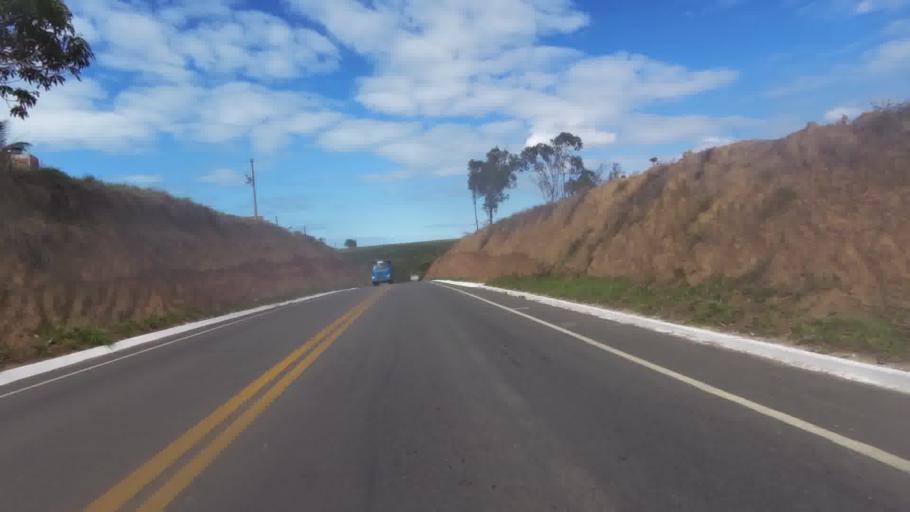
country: BR
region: Espirito Santo
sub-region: Marataizes
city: Marataizes
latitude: -21.0840
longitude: -40.8497
